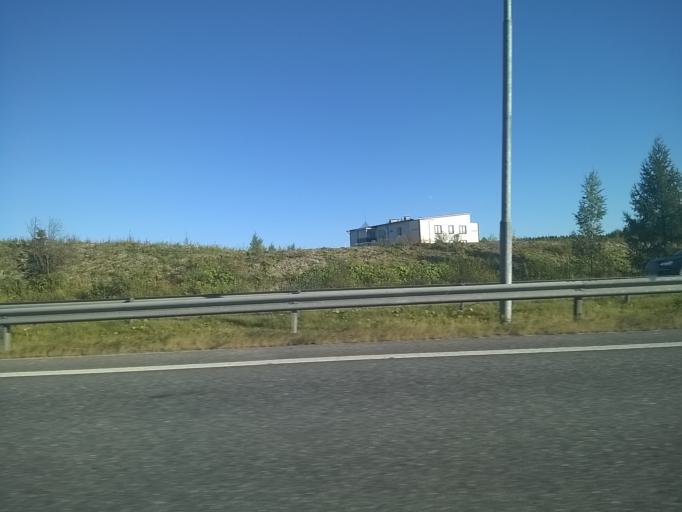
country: FI
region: Pirkanmaa
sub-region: Tampere
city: Tampere
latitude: 61.4709
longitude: 23.8600
